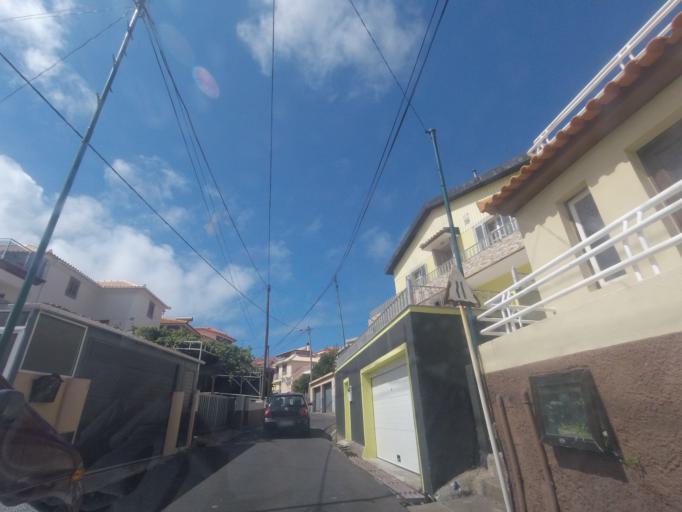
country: PT
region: Madeira
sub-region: Machico
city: Canical
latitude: 32.7406
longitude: -16.7391
